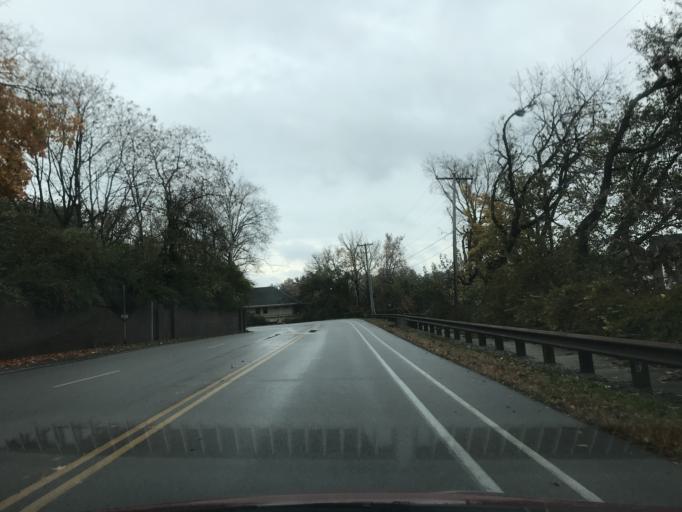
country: US
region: Indiana
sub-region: Clark County
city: Jeffersonville
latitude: 38.2466
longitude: -85.7074
